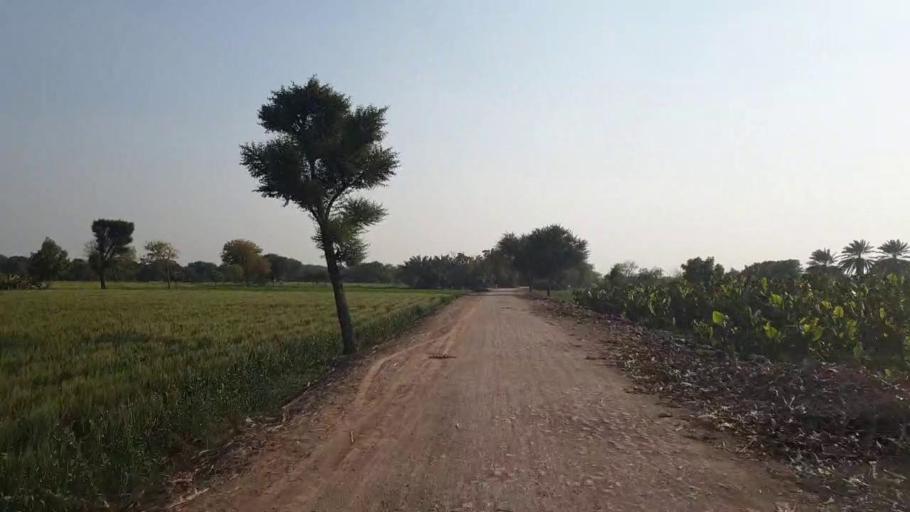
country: PK
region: Sindh
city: Mirpur Khas
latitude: 25.4116
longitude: 68.9439
